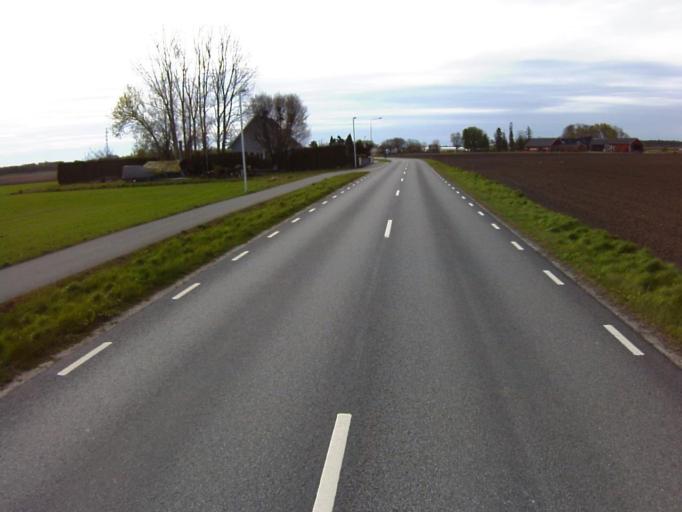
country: SE
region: Skane
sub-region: Kristianstads Kommun
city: Norra Asum
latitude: 56.0063
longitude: 14.1309
